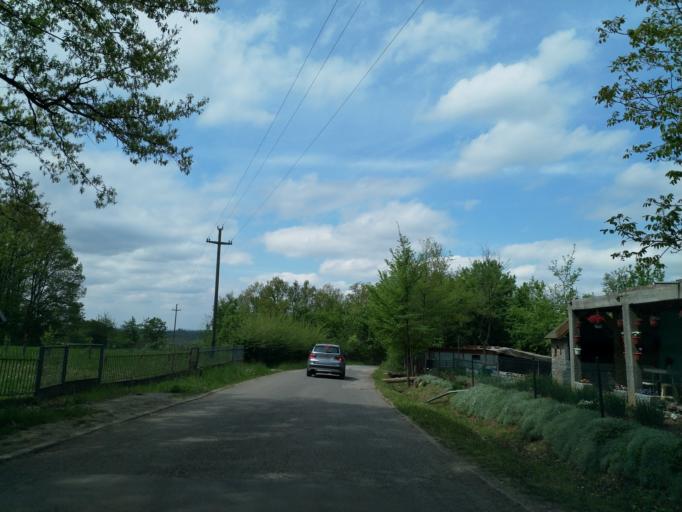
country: RS
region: Central Serbia
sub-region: Pomoravski Okrug
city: Cuprija
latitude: 43.9505
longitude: 21.4869
